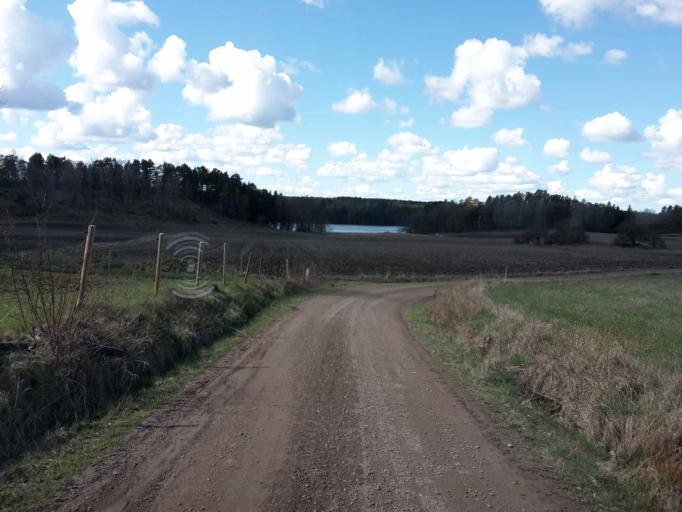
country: SE
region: OEstergoetland
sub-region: Linkopings Kommun
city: Sturefors
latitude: 58.3057
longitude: 15.8584
